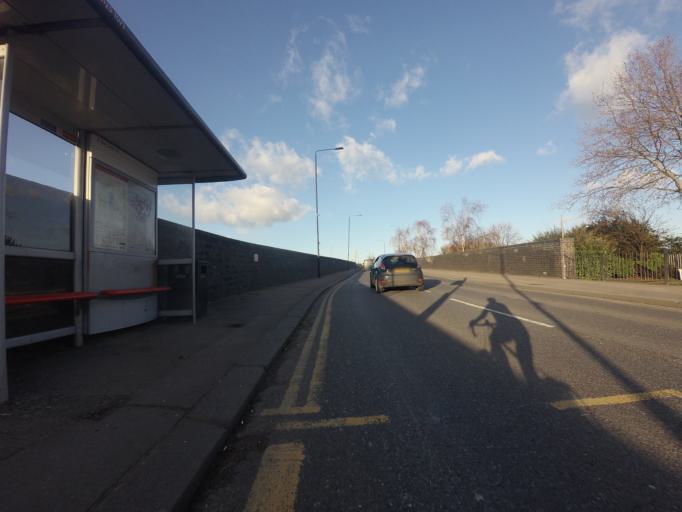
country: GB
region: England
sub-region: Greater London
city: Poplar
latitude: 51.5220
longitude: 0.0044
